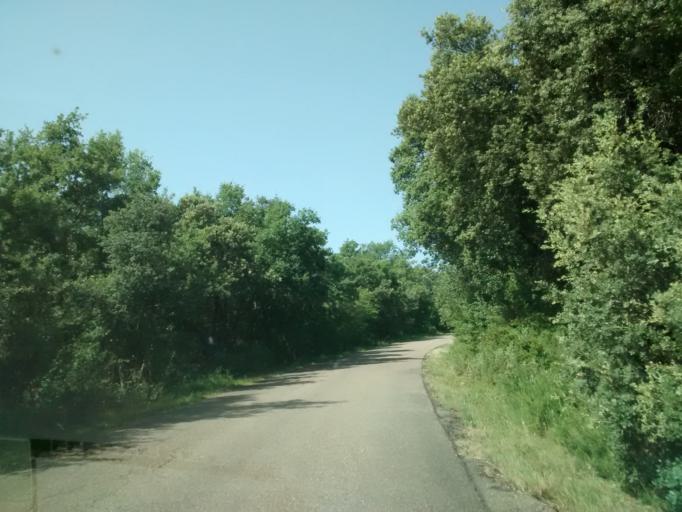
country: ES
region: Aragon
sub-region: Provincia de Zaragoza
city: Litago
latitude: 41.8011
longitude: -1.7364
